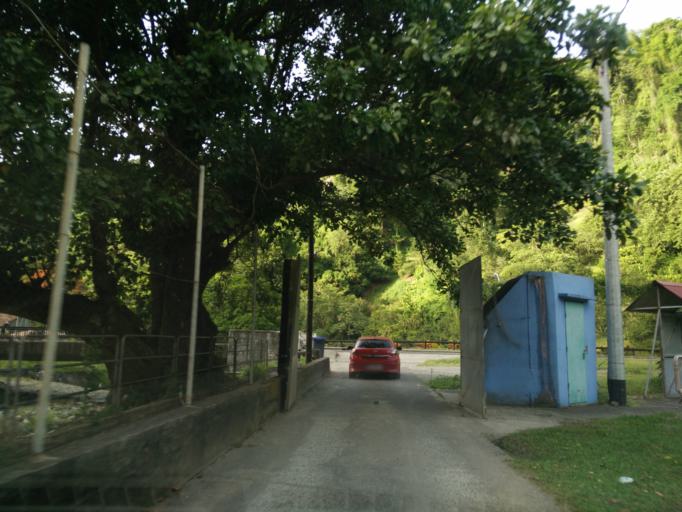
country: MQ
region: Martinique
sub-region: Martinique
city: Basse-Pointe
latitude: 14.8701
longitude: -61.1761
